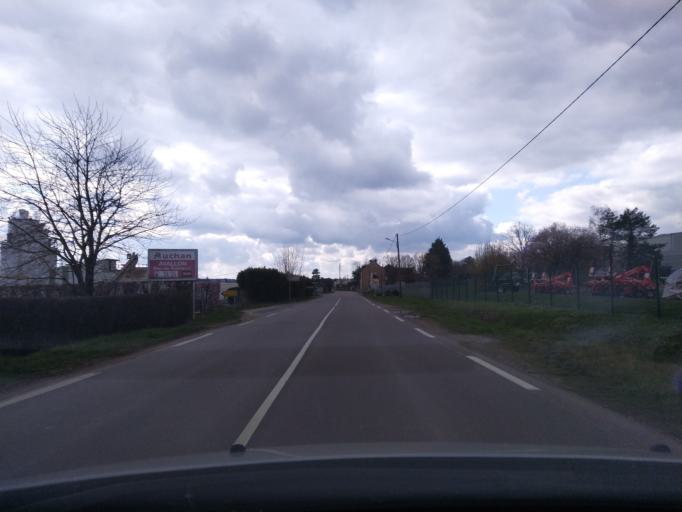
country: FR
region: Bourgogne
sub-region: Departement de l'Yonne
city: Avallon
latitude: 47.4984
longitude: 3.9267
